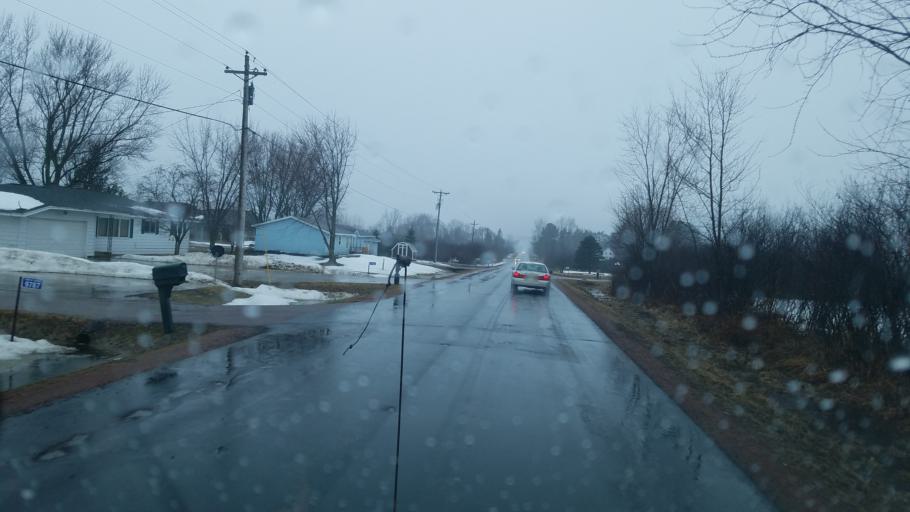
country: US
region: Wisconsin
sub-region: Wood County
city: Marshfield
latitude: 44.6771
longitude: -90.2025
